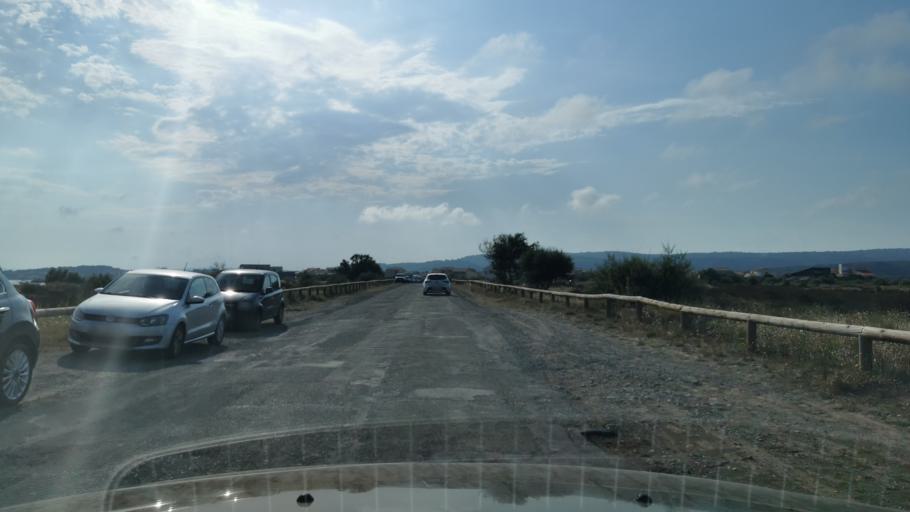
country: FR
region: Languedoc-Roussillon
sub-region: Departement de l'Aude
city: Gruissan
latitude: 43.1135
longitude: 3.1236
